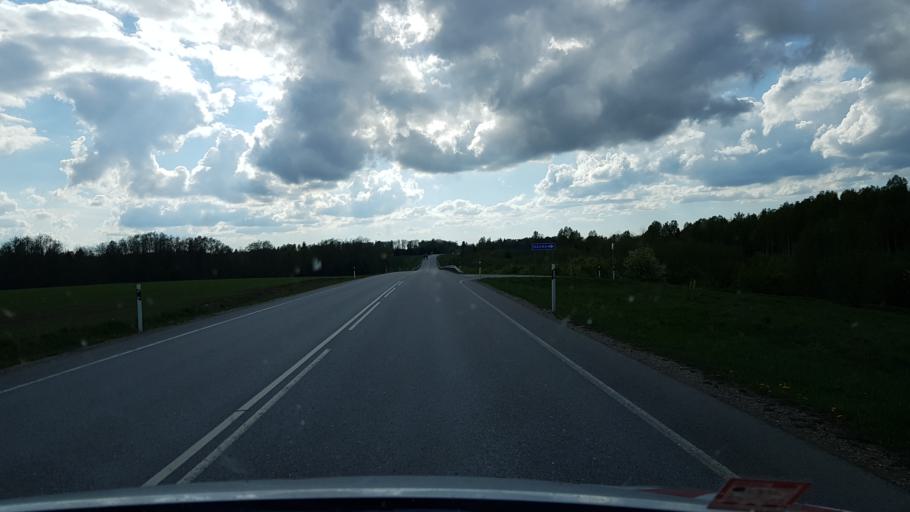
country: EE
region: Viljandimaa
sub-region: Viiratsi vald
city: Viiratsi
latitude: 58.3911
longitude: 25.7910
